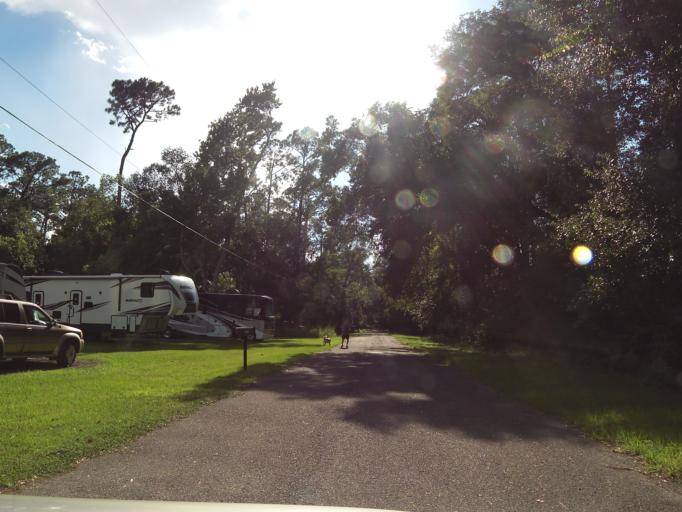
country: US
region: Florida
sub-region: Clay County
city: Orange Park
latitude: 30.2344
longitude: -81.6990
